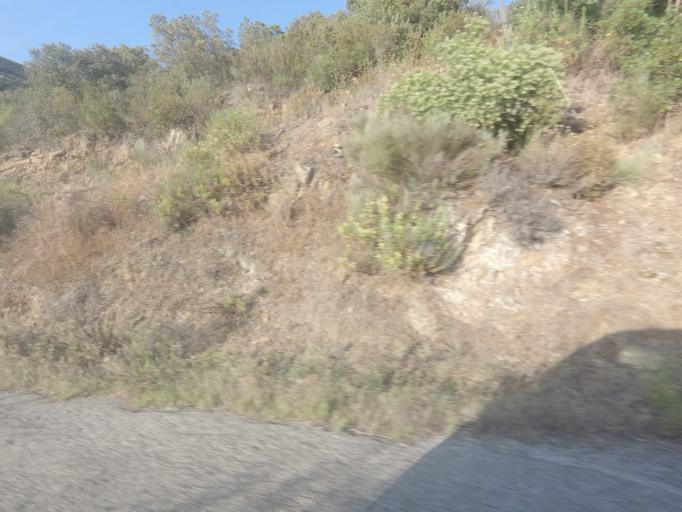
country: PT
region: Viseu
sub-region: Armamar
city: Armamar
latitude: 41.1293
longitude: -7.6737
